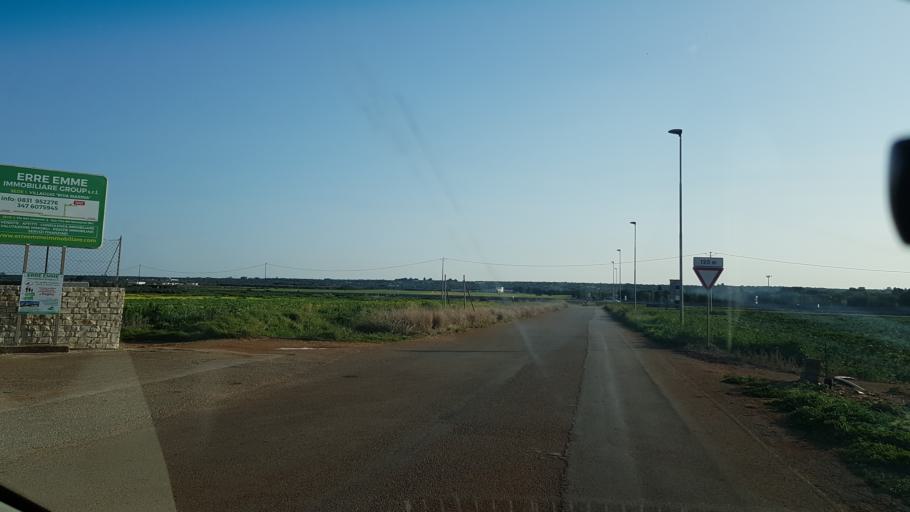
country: IT
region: Apulia
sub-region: Provincia di Brindisi
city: Carovigno
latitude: 40.7372
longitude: 17.7273
